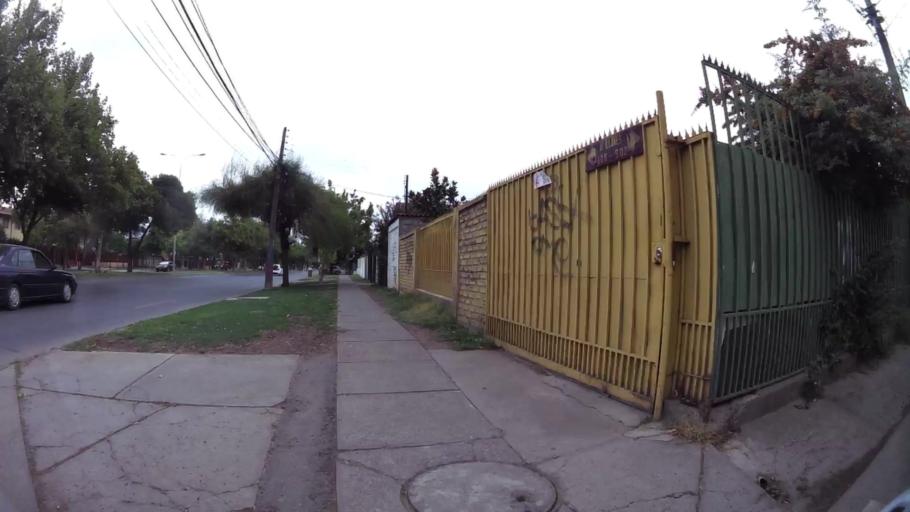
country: CL
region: O'Higgins
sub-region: Provincia de Cachapoal
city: Rancagua
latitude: -34.1604
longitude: -70.7329
